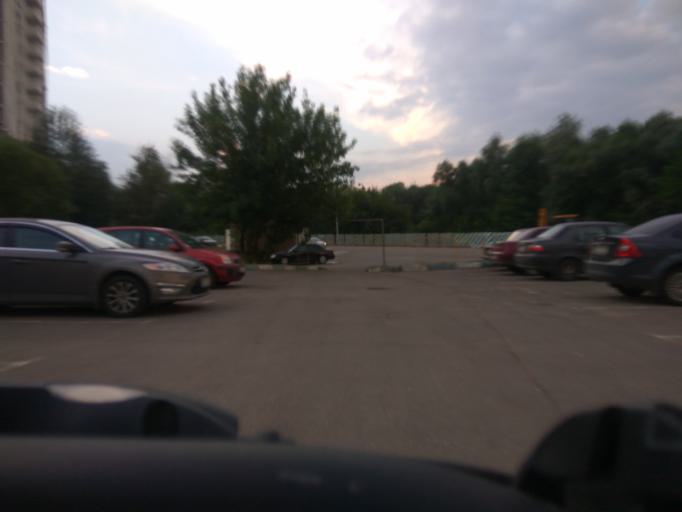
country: RU
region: Moscow
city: Brateyevo
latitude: 55.6427
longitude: 37.7757
